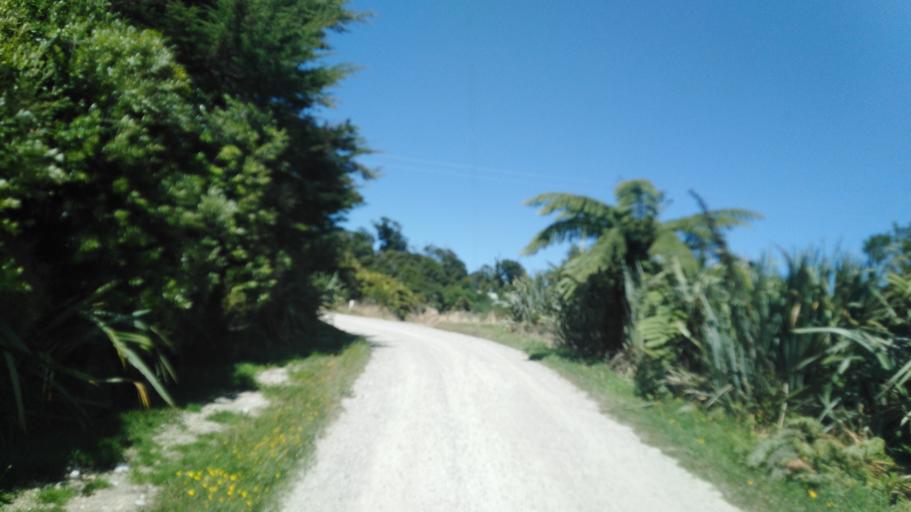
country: NZ
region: West Coast
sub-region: Buller District
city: Westport
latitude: -41.2657
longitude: 172.1134
